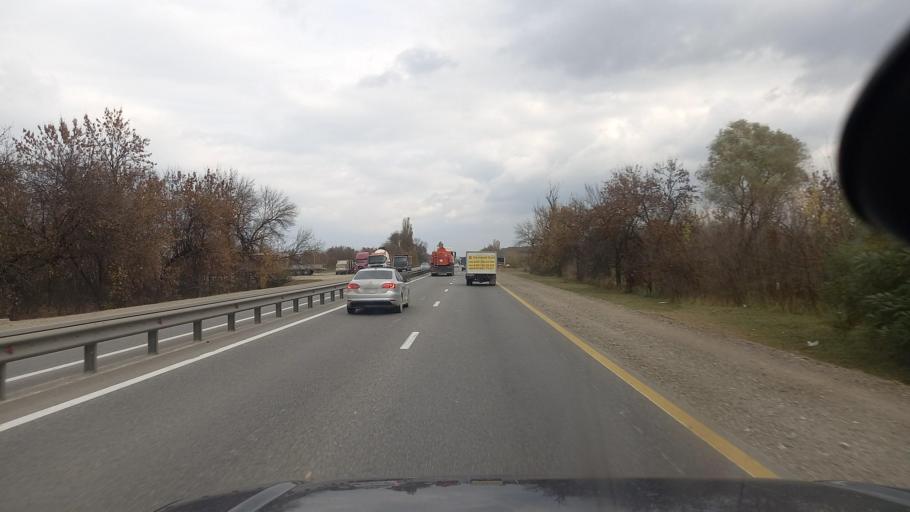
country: RU
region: Krasnodarskiy
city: Afipskiy
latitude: 44.8977
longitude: 38.8660
